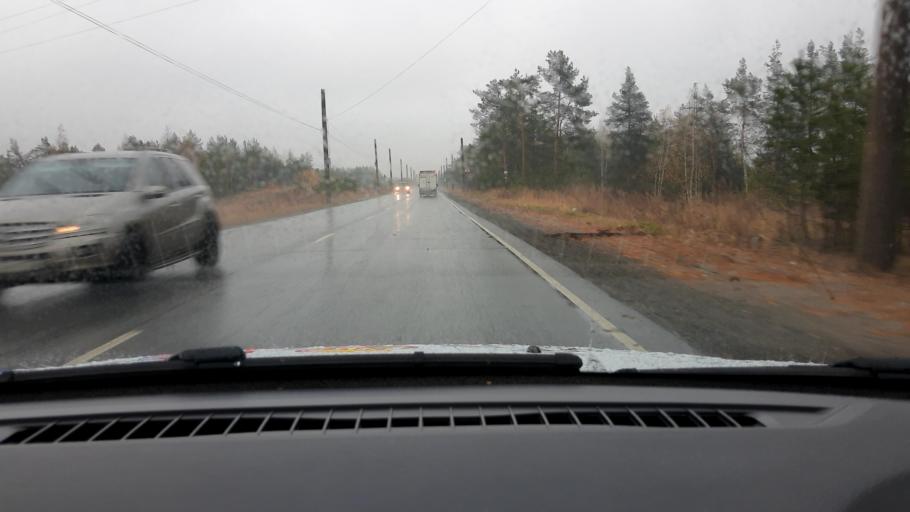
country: RU
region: Nizjnij Novgorod
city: Dzerzhinsk
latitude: 56.2679
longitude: 43.5364
